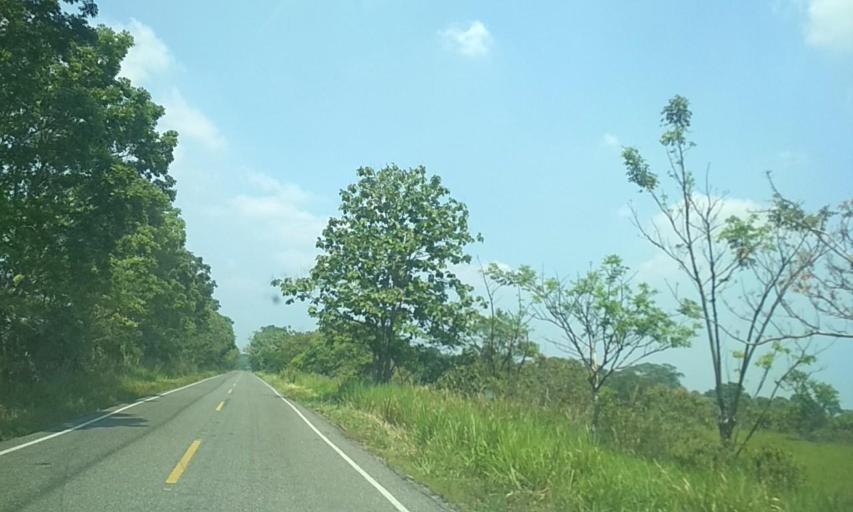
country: MX
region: Tabasco
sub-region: Huimanguillo
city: C-41 (Licenciado Carlos A. Madrazo)
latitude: 17.8476
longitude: -93.5382
